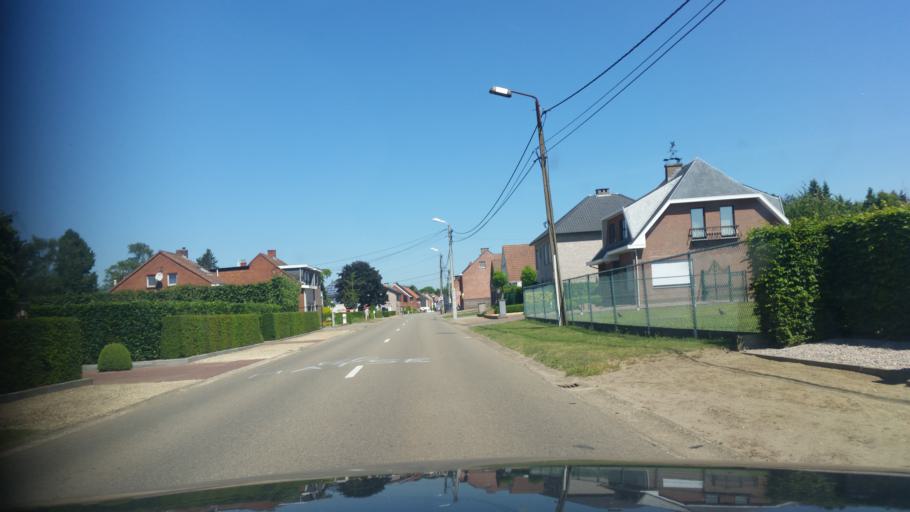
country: BE
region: Flanders
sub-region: Provincie Antwerpen
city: Meerhout
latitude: 51.1263
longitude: 5.0786
